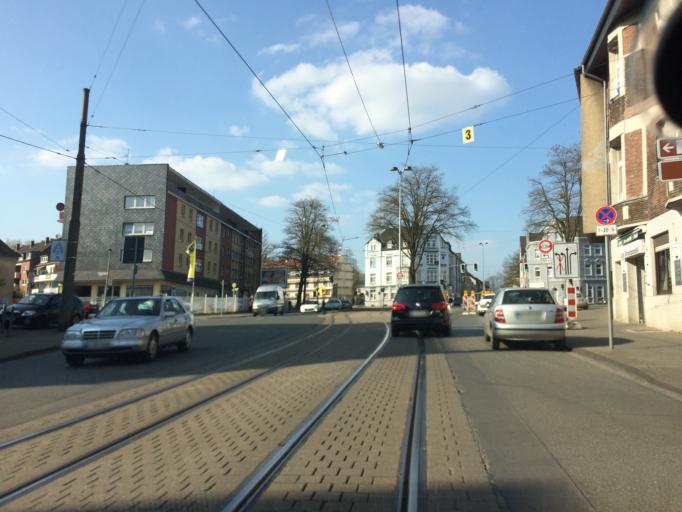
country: DE
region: North Rhine-Westphalia
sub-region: Regierungsbezirk Munster
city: Gelsenkirchen
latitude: 51.4925
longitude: 7.1229
